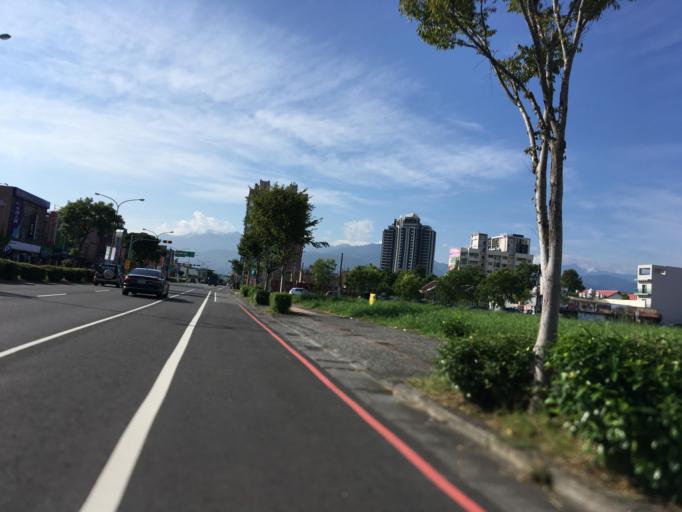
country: TW
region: Taiwan
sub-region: Yilan
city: Yilan
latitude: 24.6800
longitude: 121.7777
